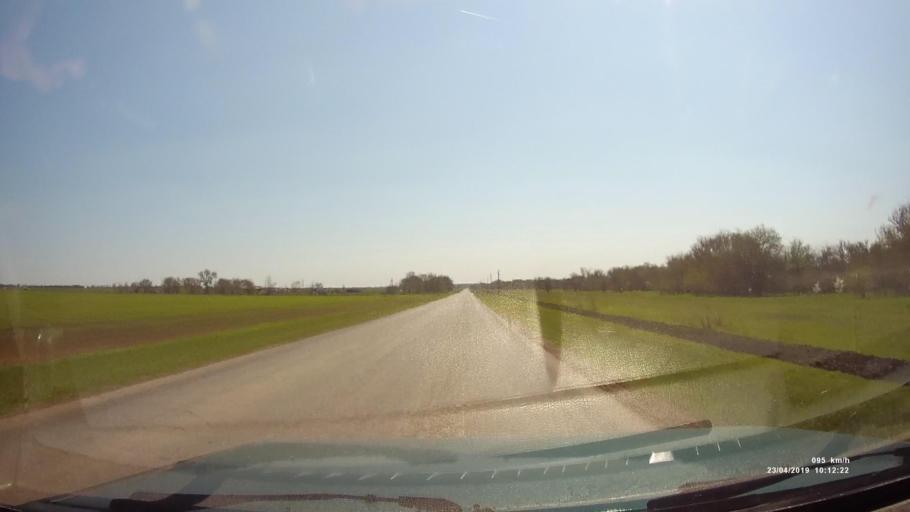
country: RU
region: Rostov
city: Sovetskoye
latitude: 46.6904
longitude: 42.3344
